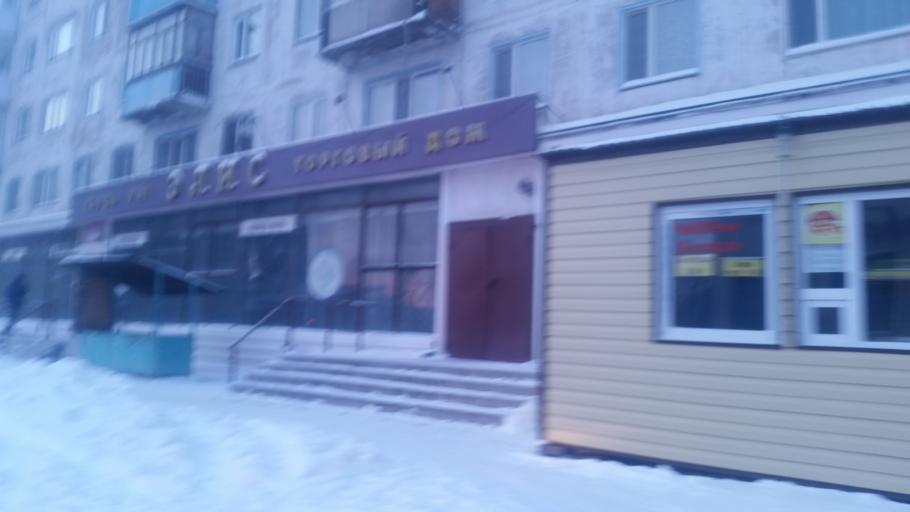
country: KZ
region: Qaraghandy
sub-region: Qaraghandy Qalasy
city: Karagandy
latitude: 49.9004
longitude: 73.0825
